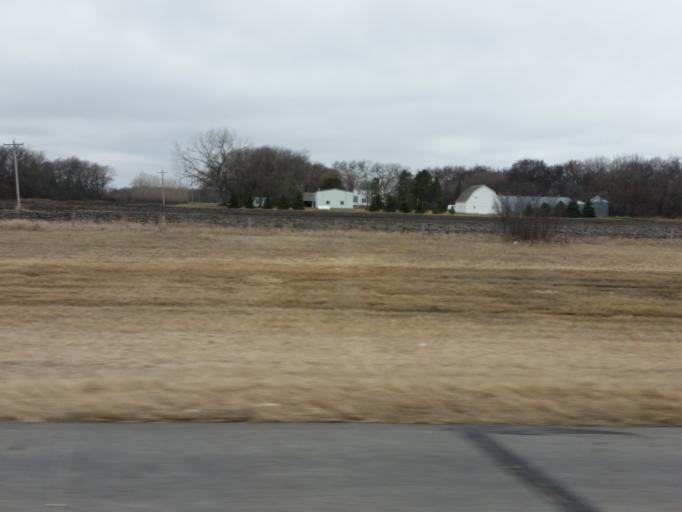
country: US
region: North Dakota
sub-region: Cass County
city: Horace
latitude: 46.5512
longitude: -96.8228
